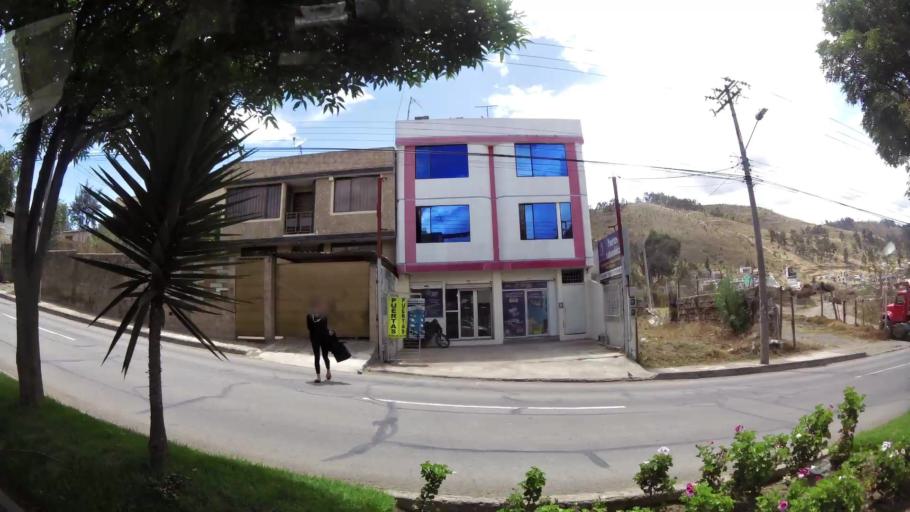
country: EC
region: Tungurahua
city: Ambato
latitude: -1.2647
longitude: -78.6383
